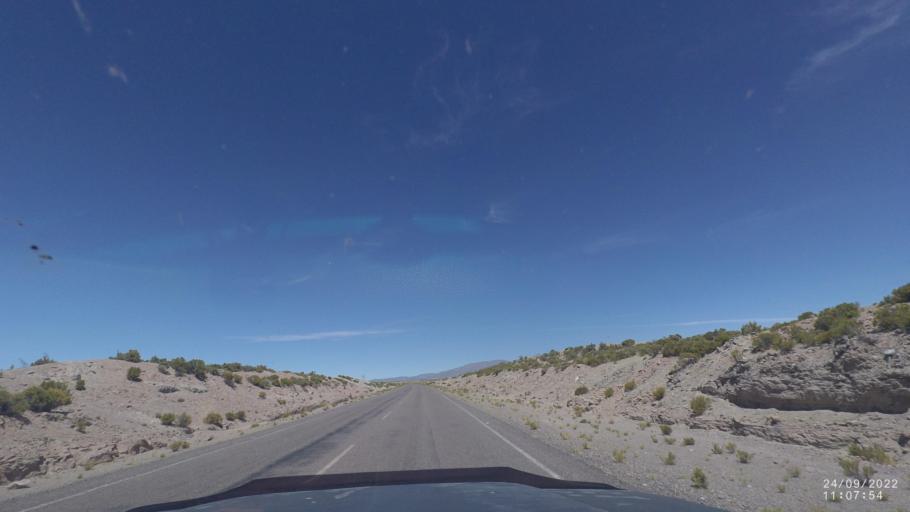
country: BO
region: Oruro
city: Challapata
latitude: -19.4804
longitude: -67.4362
